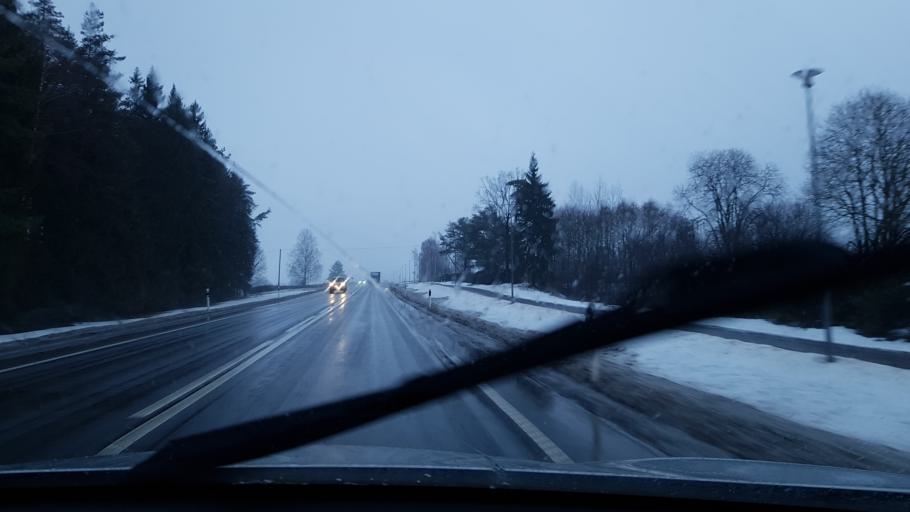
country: EE
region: Jaervamaa
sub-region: Tueri vald
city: Tueri
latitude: 58.8352
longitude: 25.4713
